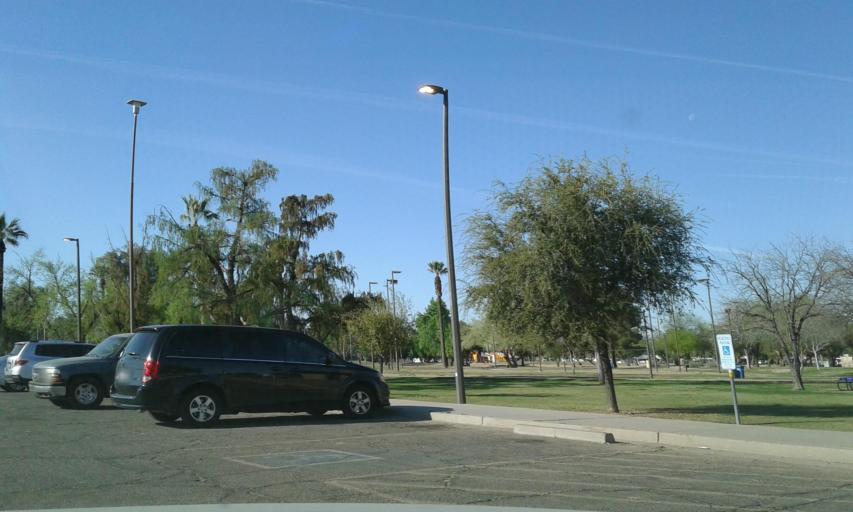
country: US
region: Arizona
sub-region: Maricopa County
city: Glendale
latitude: 33.5335
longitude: -112.1052
